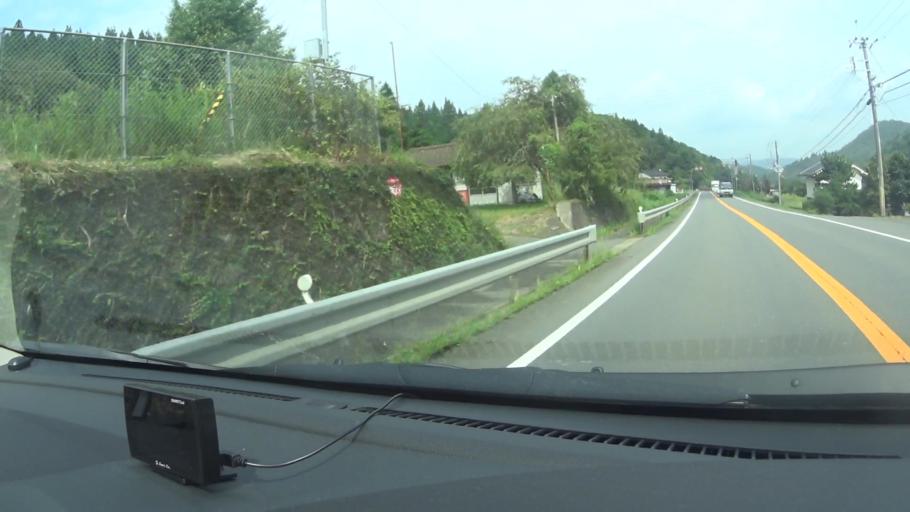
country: JP
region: Hyogo
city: Sasayama
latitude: 35.1564
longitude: 135.3544
